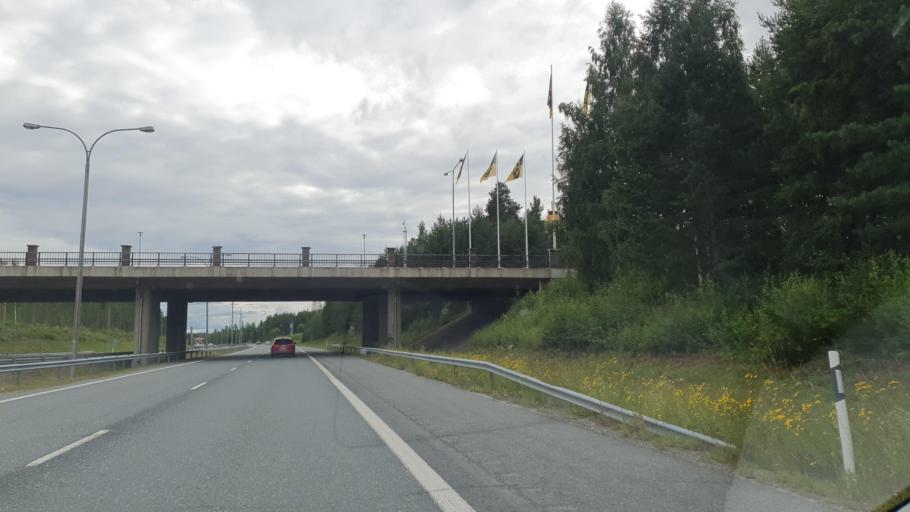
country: FI
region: Northern Savo
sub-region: Ylae-Savo
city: Iisalmi
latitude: 63.5469
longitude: 27.2508
